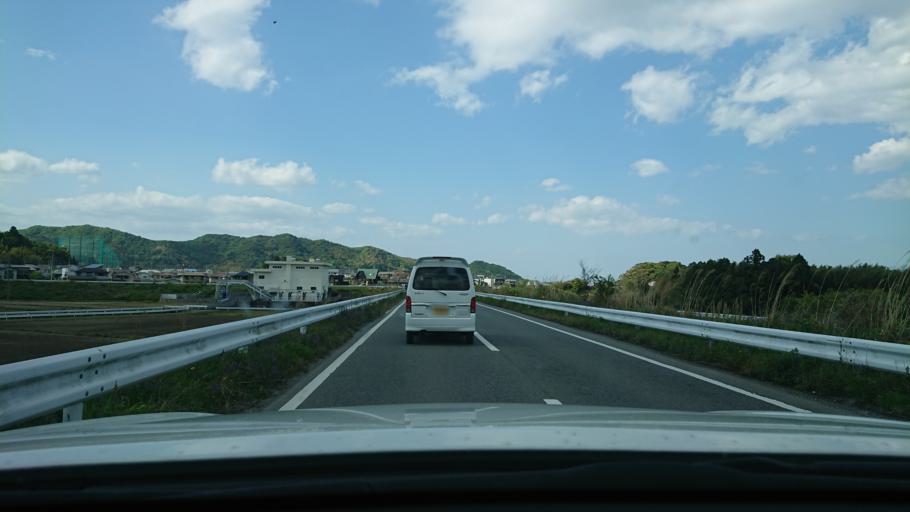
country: JP
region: Tokushima
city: Komatsushimacho
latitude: 33.9980
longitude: 134.5476
